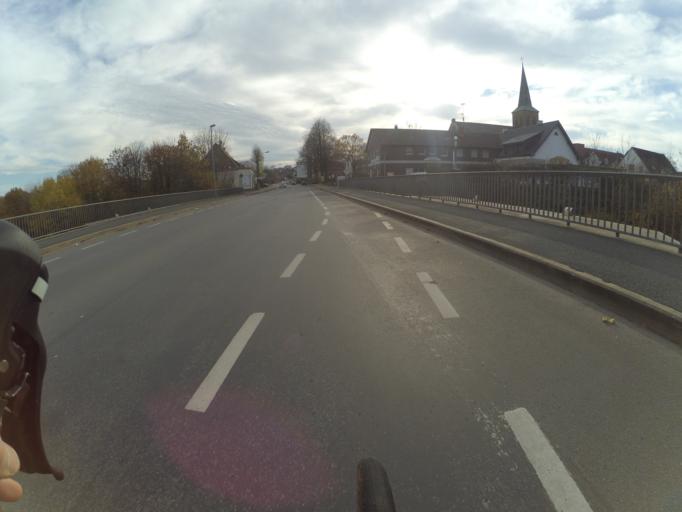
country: DE
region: North Rhine-Westphalia
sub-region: Regierungsbezirk Munster
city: Tecklenburg
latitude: 52.2627
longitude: 7.7894
